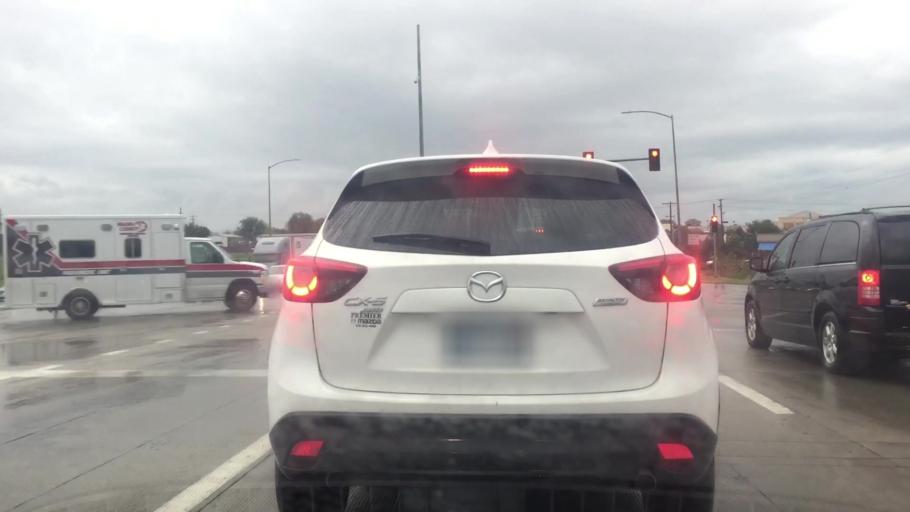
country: US
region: Kansas
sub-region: Johnson County
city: Olathe
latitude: 38.8531
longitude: -94.8159
